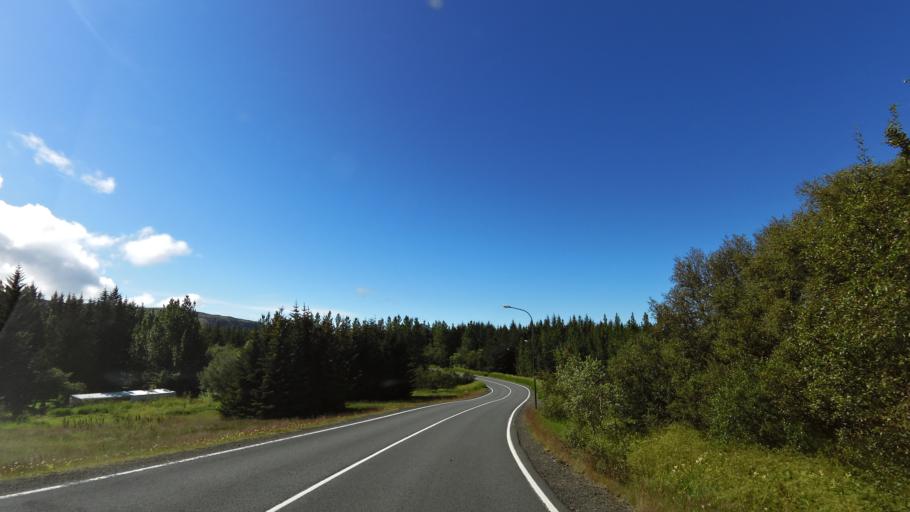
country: IS
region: Capital Region
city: Mosfellsbaer
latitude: 64.1620
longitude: -21.6676
